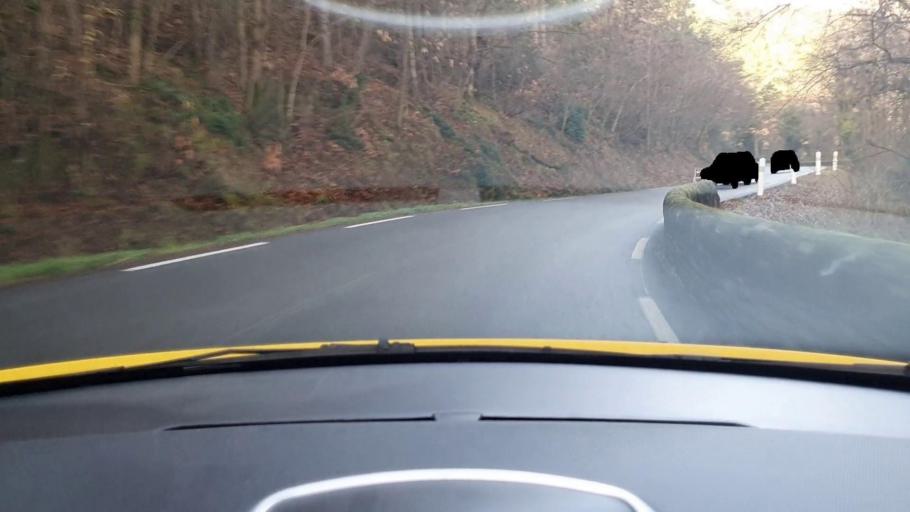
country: FR
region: Languedoc-Roussillon
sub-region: Departement du Gard
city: Branoux-les-Taillades
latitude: 44.3340
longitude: 3.9582
